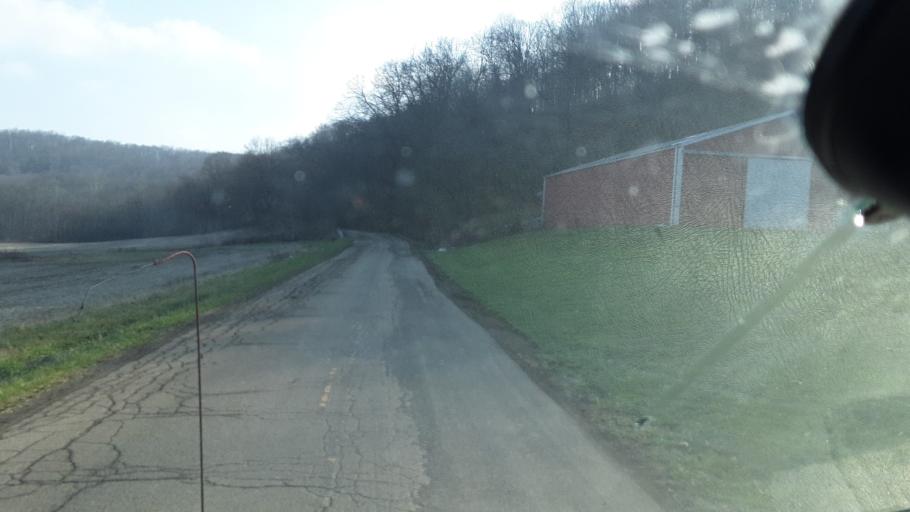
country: US
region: Ohio
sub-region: Knox County
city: Oak Hill
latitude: 40.4273
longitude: -82.2001
